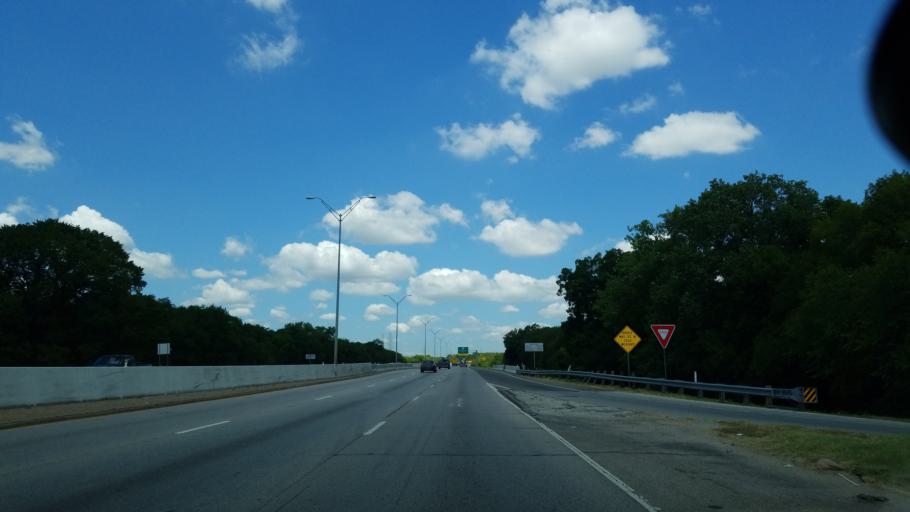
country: US
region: Texas
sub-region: Dallas County
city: Dallas
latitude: 32.7457
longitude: -96.7297
